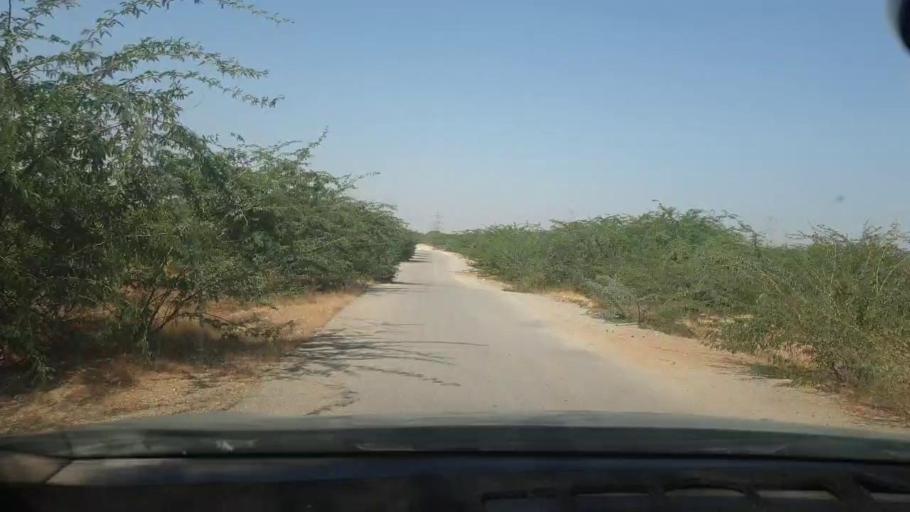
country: PK
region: Sindh
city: Malir Cantonment
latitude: 25.1606
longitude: 67.1624
